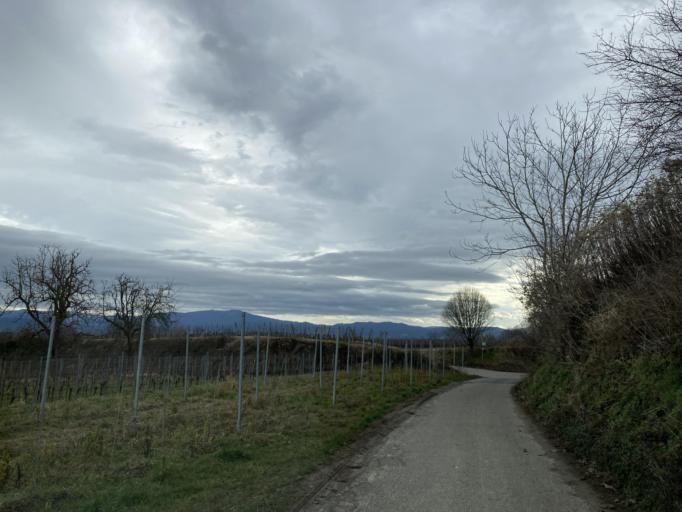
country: DE
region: Baden-Wuerttemberg
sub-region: Freiburg Region
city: Bahlingen
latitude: 48.1109
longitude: 7.7208
